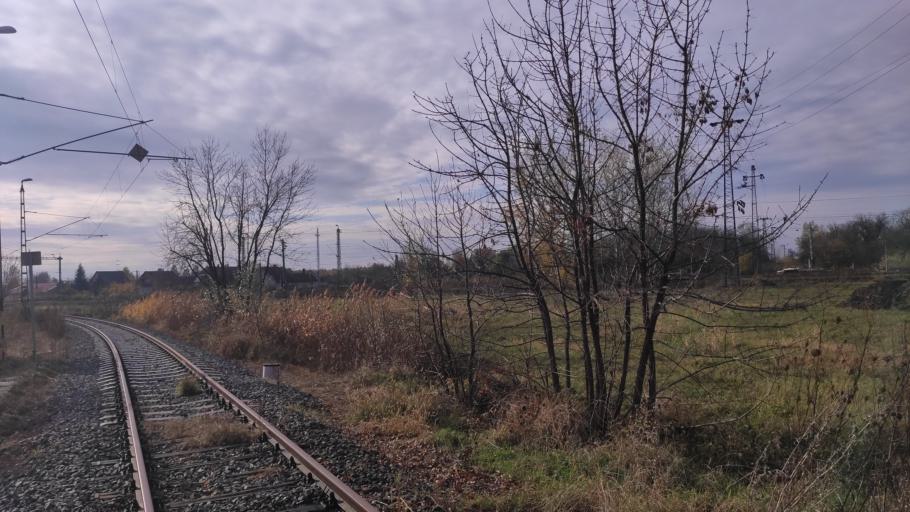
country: HU
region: Bekes
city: Mezobereny
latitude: 46.7621
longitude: 21.0374
